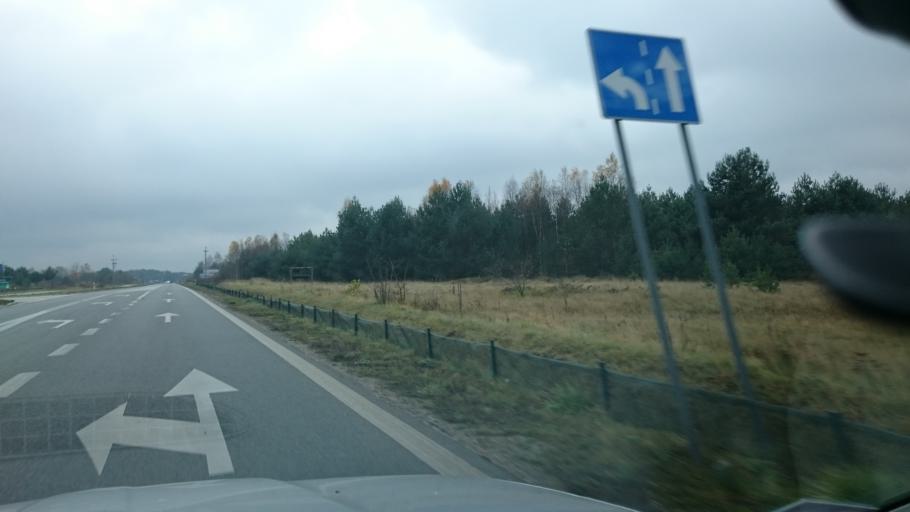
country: PL
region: Swietokrzyskie
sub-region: Powiat konecki
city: Konskie
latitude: 51.1355
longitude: 20.3627
